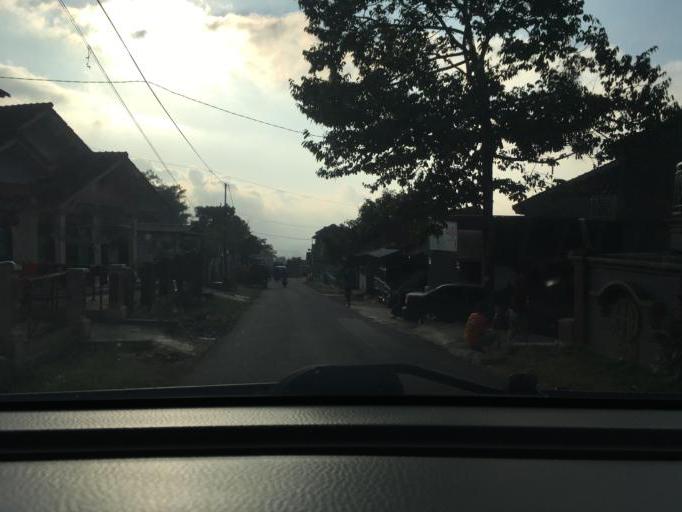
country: ID
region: West Java
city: Nagarakembang
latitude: -7.0362
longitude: 108.3255
